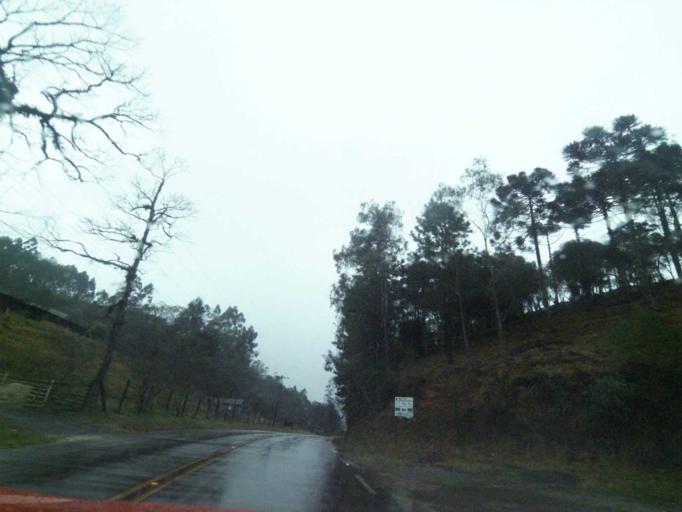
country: BR
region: Santa Catarina
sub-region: Anitapolis
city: Anitapolis
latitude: -27.8226
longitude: -49.0492
